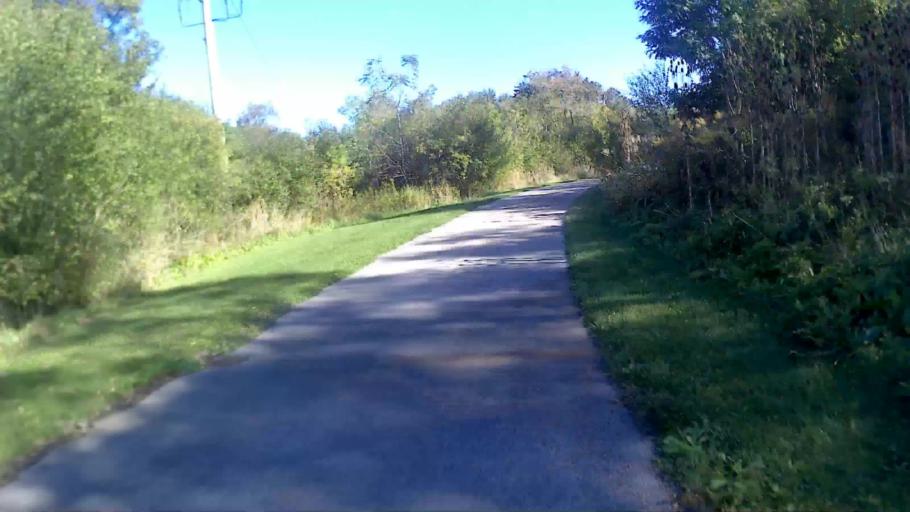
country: US
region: Illinois
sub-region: DuPage County
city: Addison
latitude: 41.9383
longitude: -87.9862
